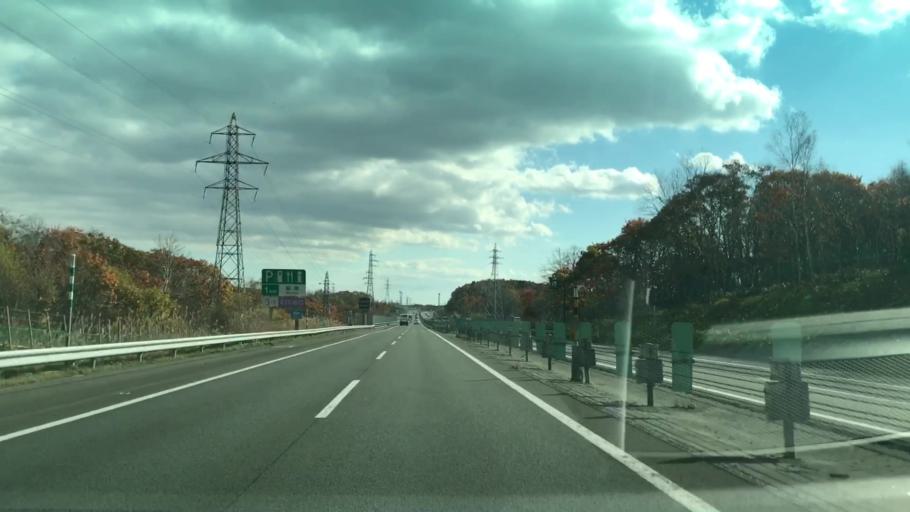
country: JP
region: Hokkaido
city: Kitahiroshima
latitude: 42.9598
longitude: 141.5016
